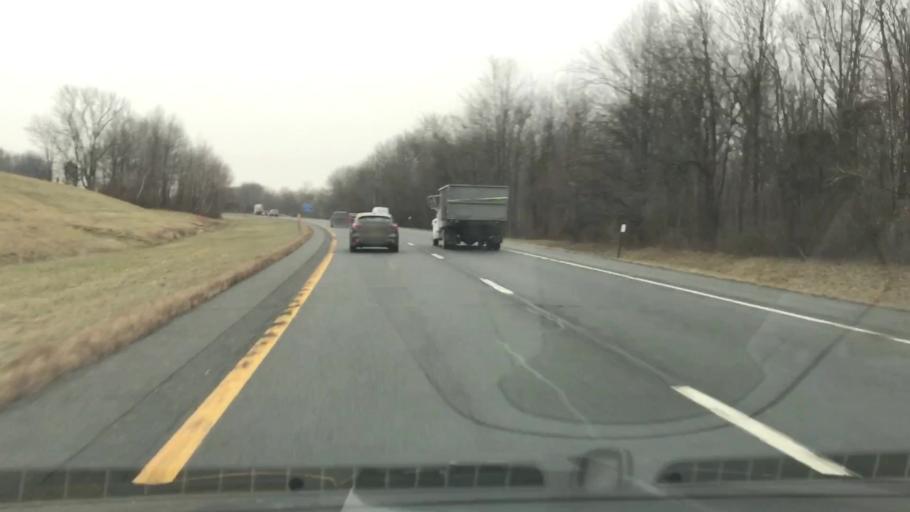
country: US
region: New York
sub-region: Orange County
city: Otisville
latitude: 41.3972
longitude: -74.5449
